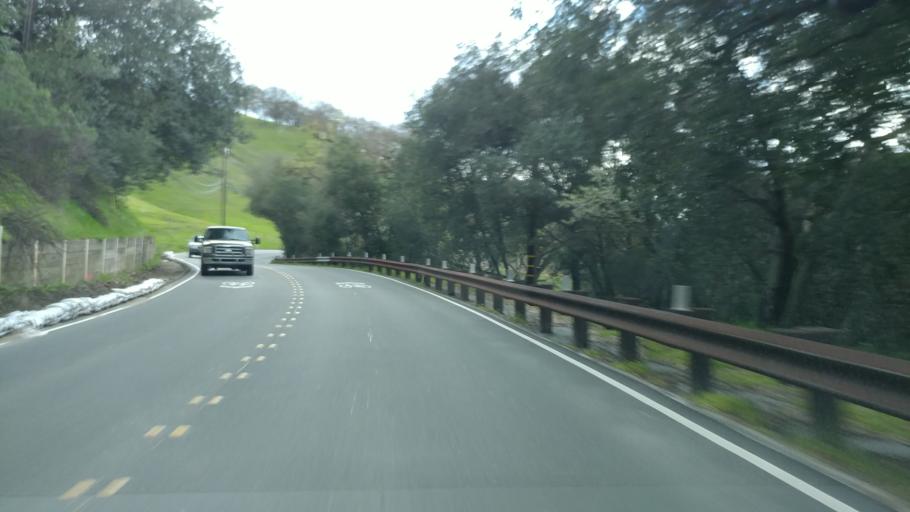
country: US
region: California
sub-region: Contra Costa County
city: Diablo
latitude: 37.8338
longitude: -121.9642
